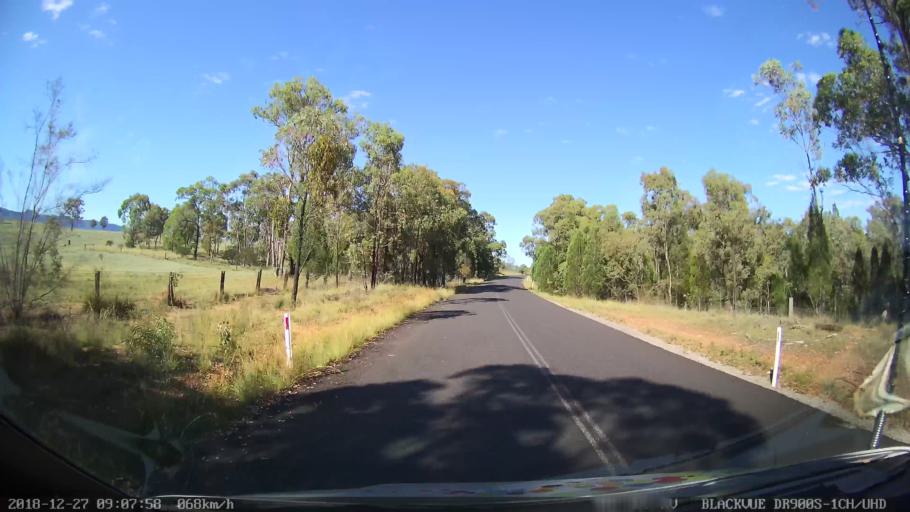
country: AU
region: New South Wales
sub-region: Lithgow
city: Portland
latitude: -33.1331
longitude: 150.1528
